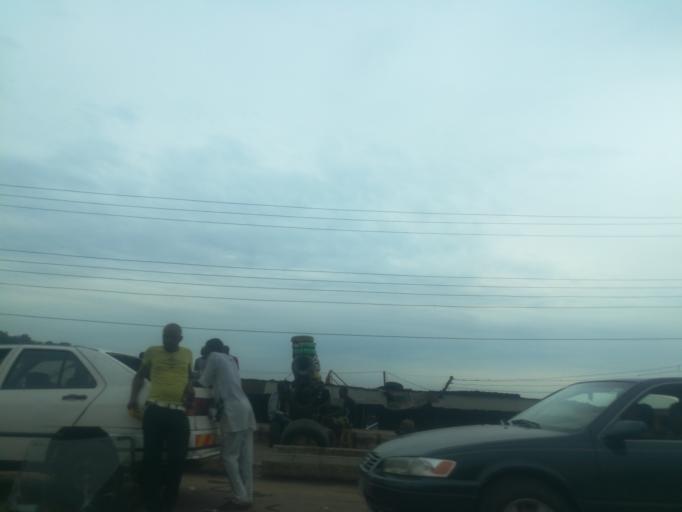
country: NG
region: Oyo
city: Ibadan
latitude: 7.3970
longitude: 3.9219
